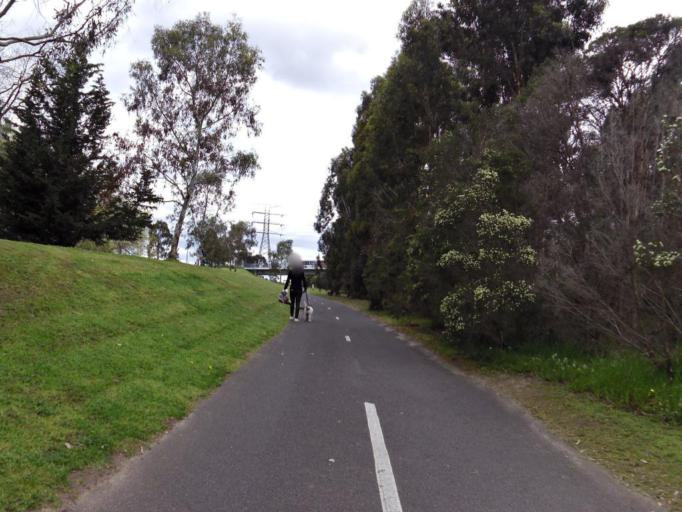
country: AU
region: Victoria
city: Glenferrie
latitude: -37.8475
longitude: 145.0428
